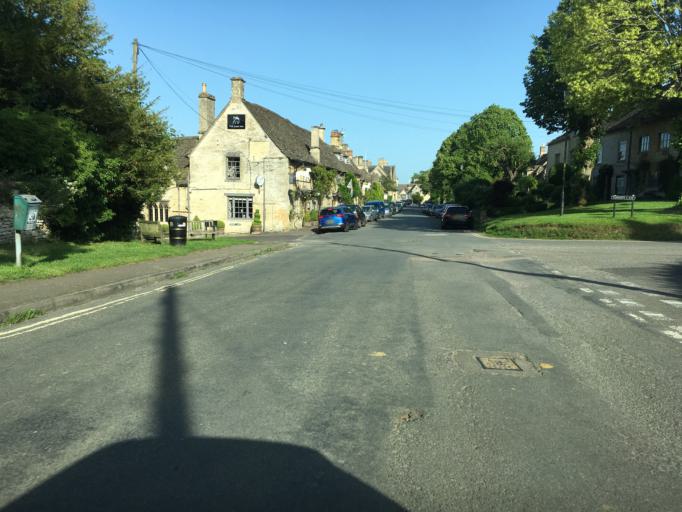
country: GB
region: England
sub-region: Oxfordshire
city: Burford
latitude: 51.8083
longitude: -1.6400
